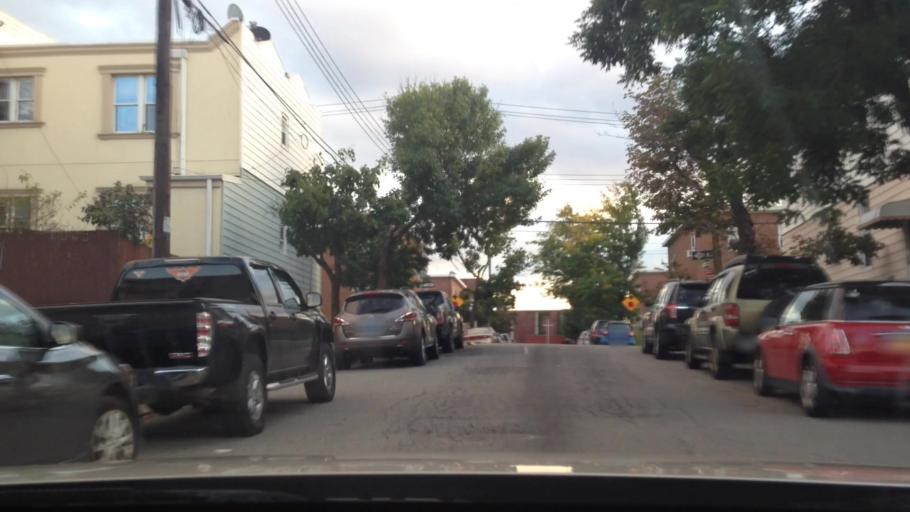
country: US
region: New York
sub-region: Queens County
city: Long Island City
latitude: 40.7242
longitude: -73.9063
